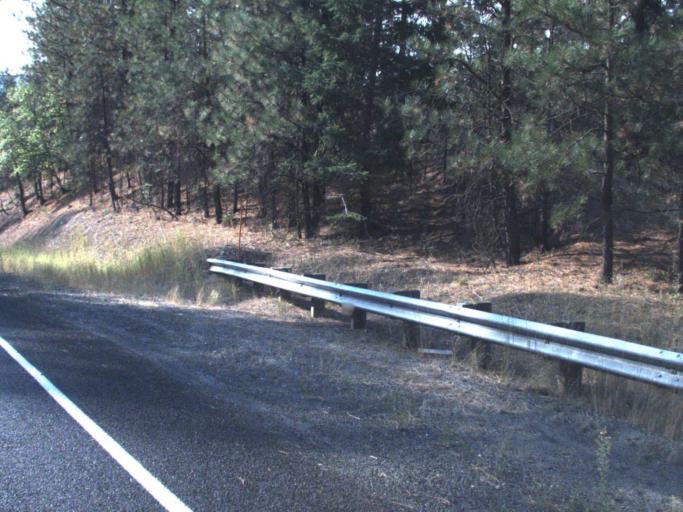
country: US
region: Washington
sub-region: Spokane County
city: Deer Park
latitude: 47.8729
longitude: -117.7079
